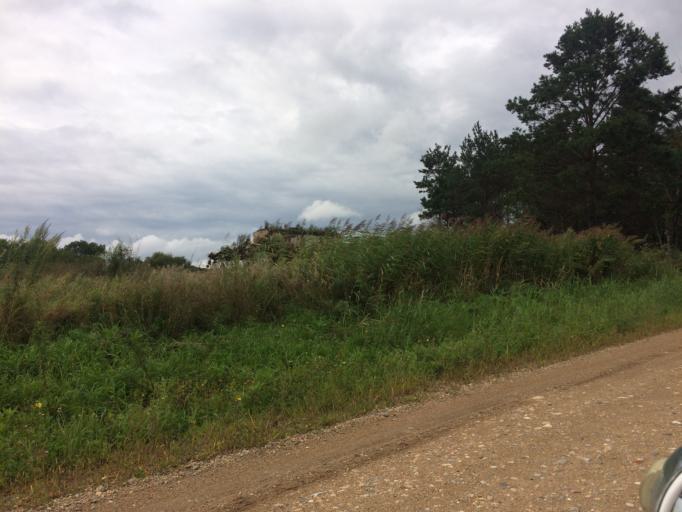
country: RU
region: Primorskiy
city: Lazo
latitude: 45.8200
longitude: 133.6444
